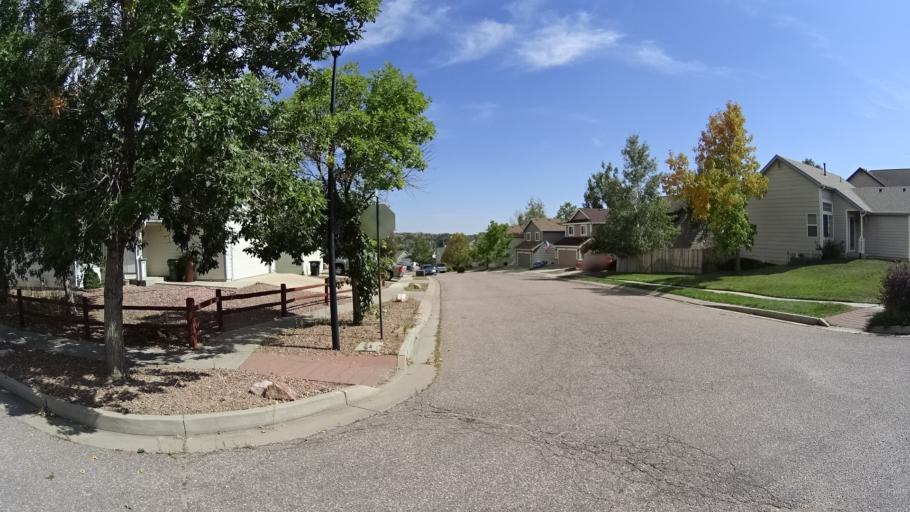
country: US
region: Colorado
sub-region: El Paso County
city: Cimarron Hills
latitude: 38.9023
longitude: -104.7124
